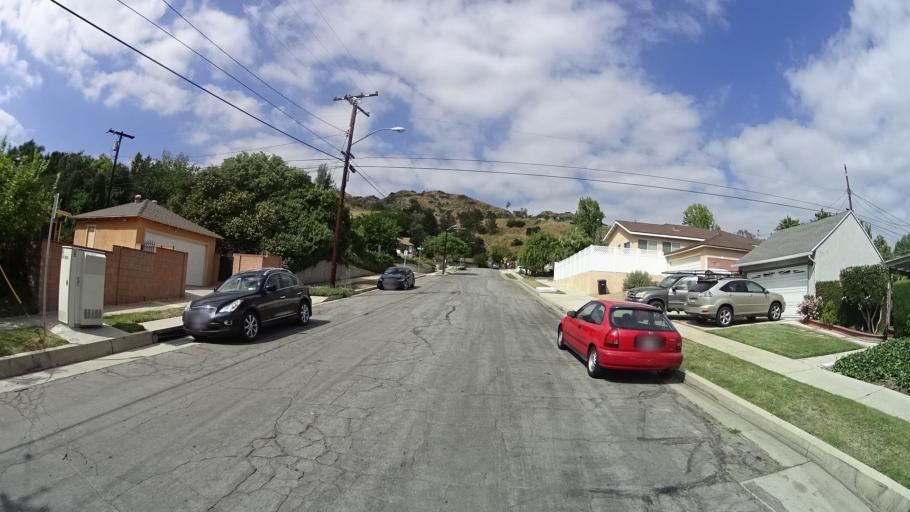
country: US
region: California
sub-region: Los Angeles County
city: Burbank
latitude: 34.2015
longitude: -118.3196
